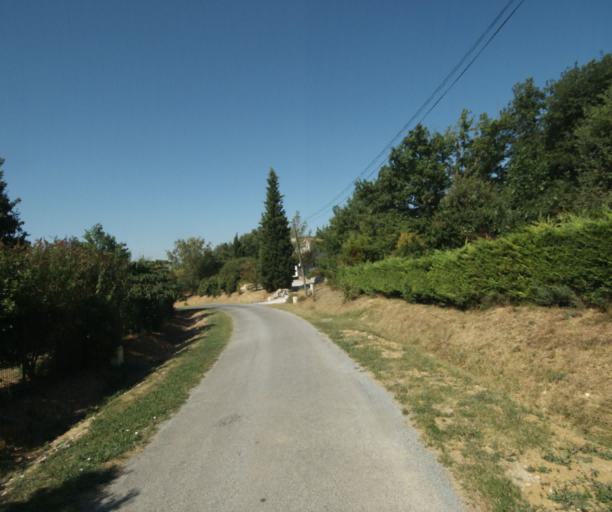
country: FR
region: Midi-Pyrenees
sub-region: Departement de la Haute-Garonne
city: Saint-Felix-Lauragais
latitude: 43.4991
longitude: 1.9385
